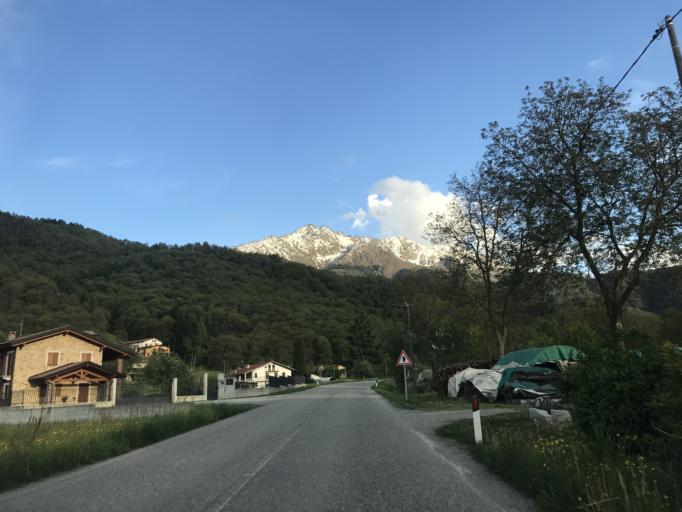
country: IT
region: Piedmont
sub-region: Provincia di Cuneo
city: Boves
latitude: 44.3074
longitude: 7.5711
